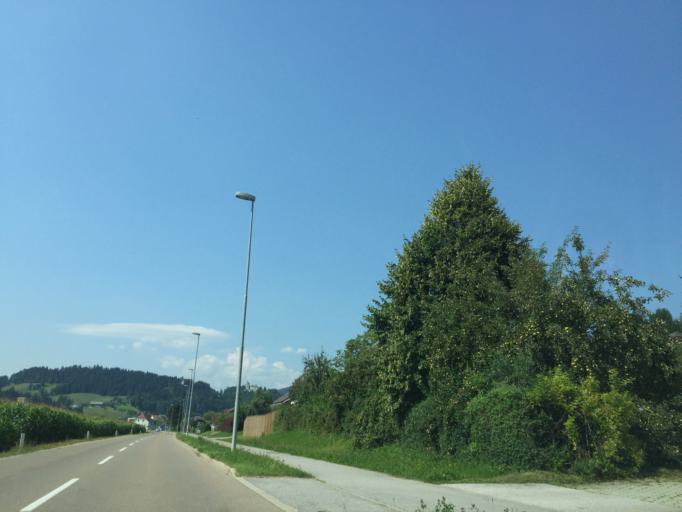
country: SI
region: Slovenj Gradec
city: Slovenj Gradec
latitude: 46.4916
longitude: 15.0737
